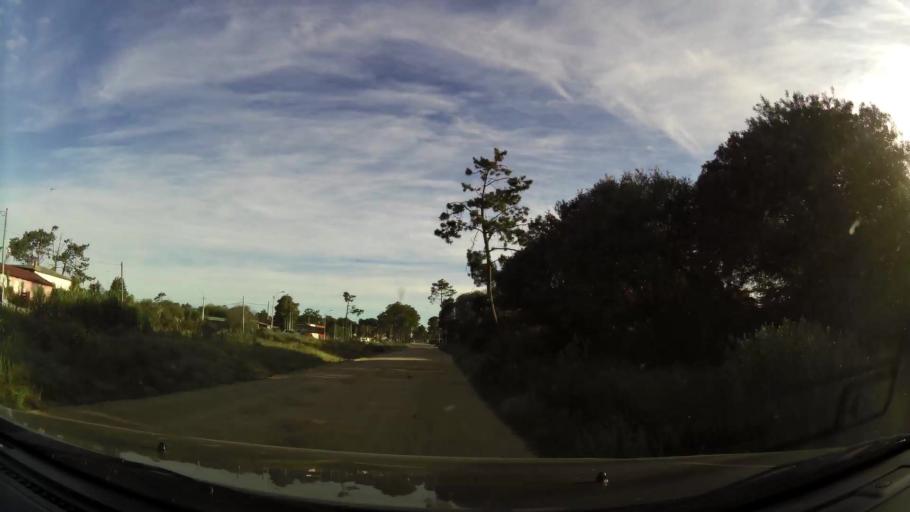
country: UY
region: Canelones
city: Empalme Olmos
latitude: -34.7757
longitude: -55.8638
